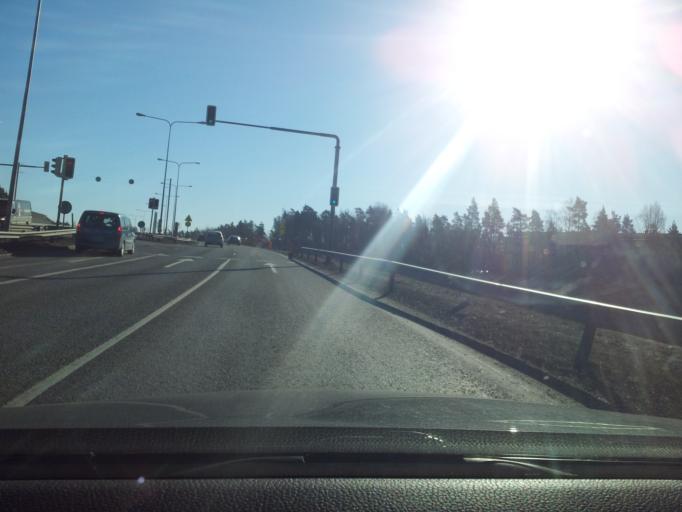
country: FI
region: Uusimaa
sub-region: Helsinki
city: Vantaa
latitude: 60.2303
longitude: 25.0534
